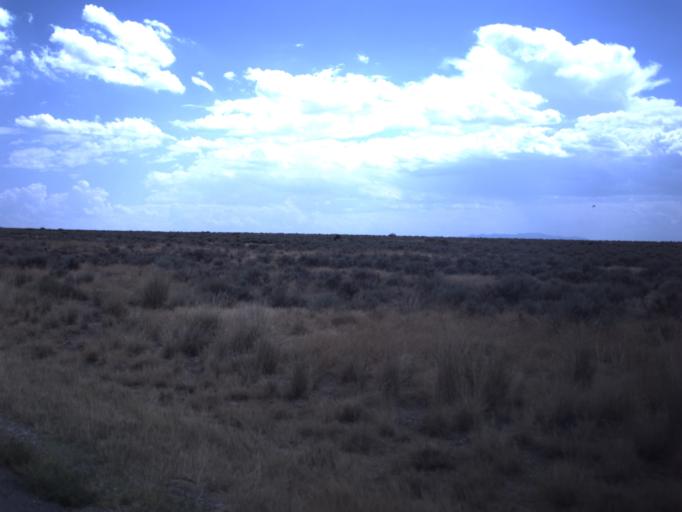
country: US
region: Utah
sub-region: Tooele County
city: Tooele
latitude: 40.3636
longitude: -112.3369
